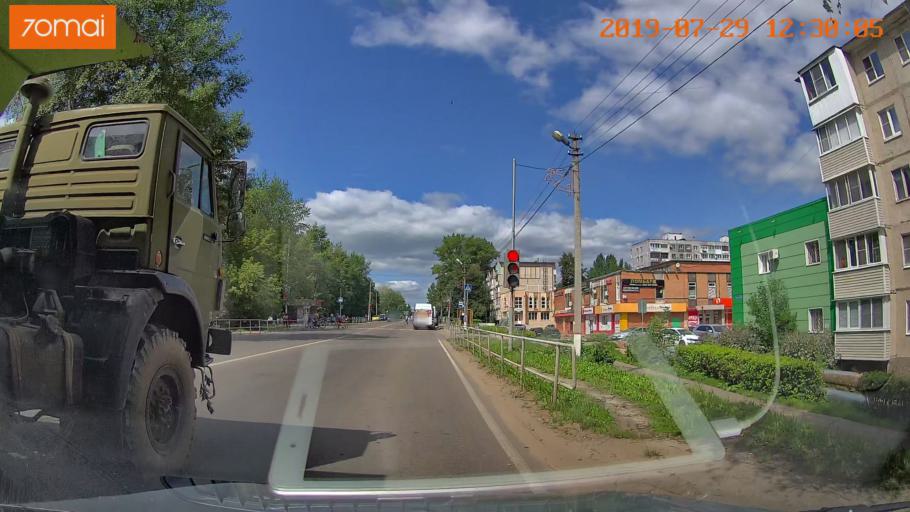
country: RU
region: Moskovskaya
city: Voskresensk
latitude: 55.3147
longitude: 38.6519
